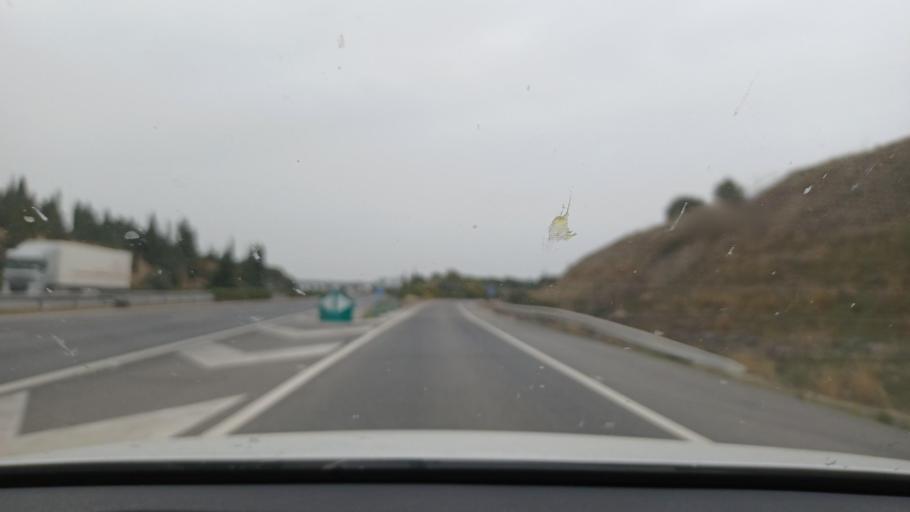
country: ES
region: Catalonia
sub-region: Provincia de Tarragona
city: Amposta
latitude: 40.7304
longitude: 0.5799
